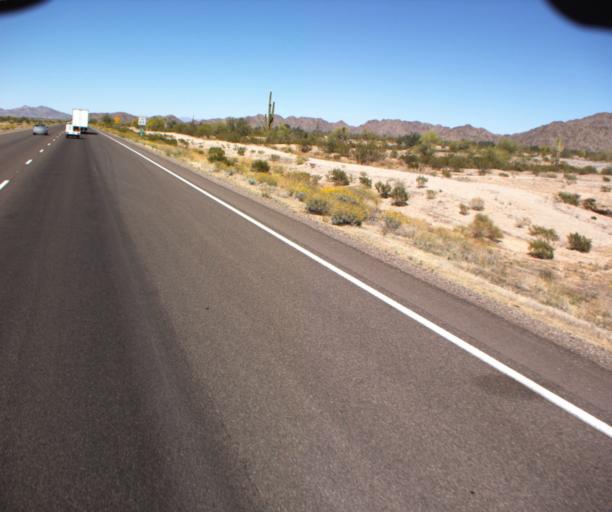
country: US
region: Arizona
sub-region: Maricopa County
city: Gila Bend
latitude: 33.1323
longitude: -112.6501
